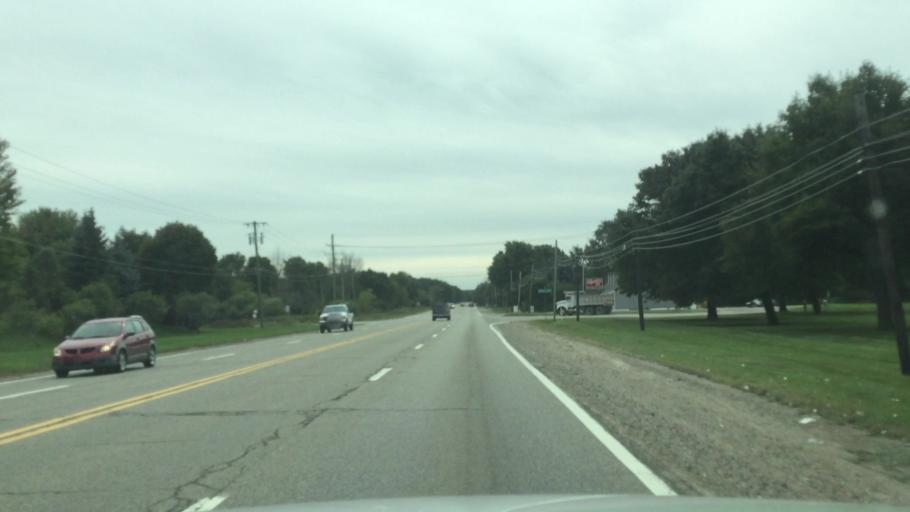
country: US
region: Michigan
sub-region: Oakland County
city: Clarkston
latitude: 42.7744
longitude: -83.4934
